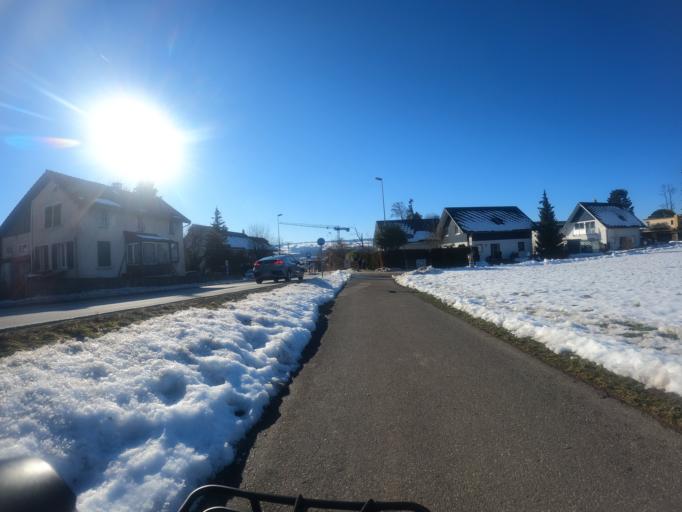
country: CH
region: Zurich
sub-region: Bezirk Affoltern
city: Ottenbach
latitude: 47.2846
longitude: 8.4099
